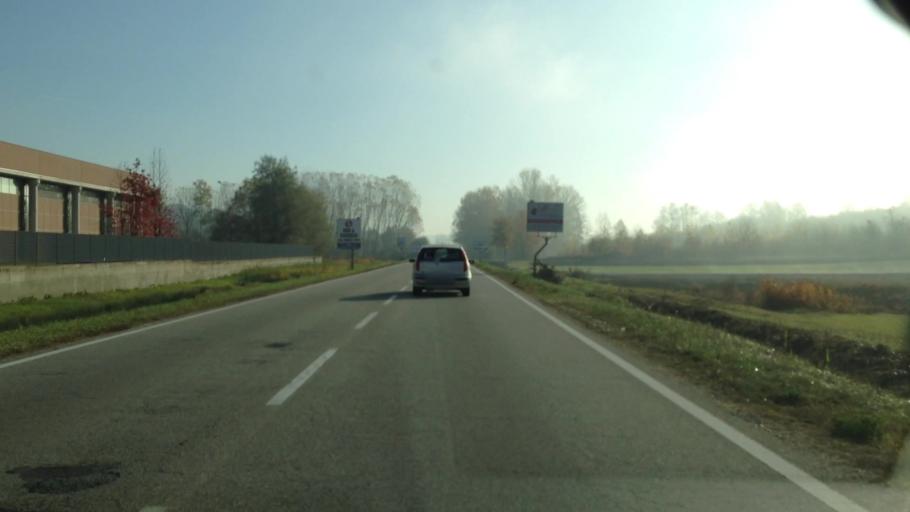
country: IT
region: Piedmont
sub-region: Provincia di Asti
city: Vigliano d'Asti
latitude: 44.8247
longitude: 8.2177
